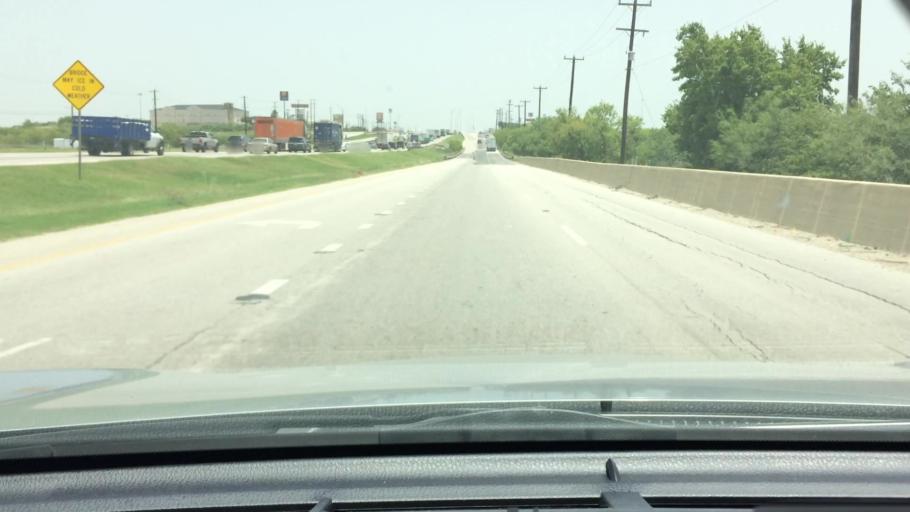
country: US
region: Texas
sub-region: Bexar County
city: Kirby
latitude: 29.4416
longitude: -98.3706
